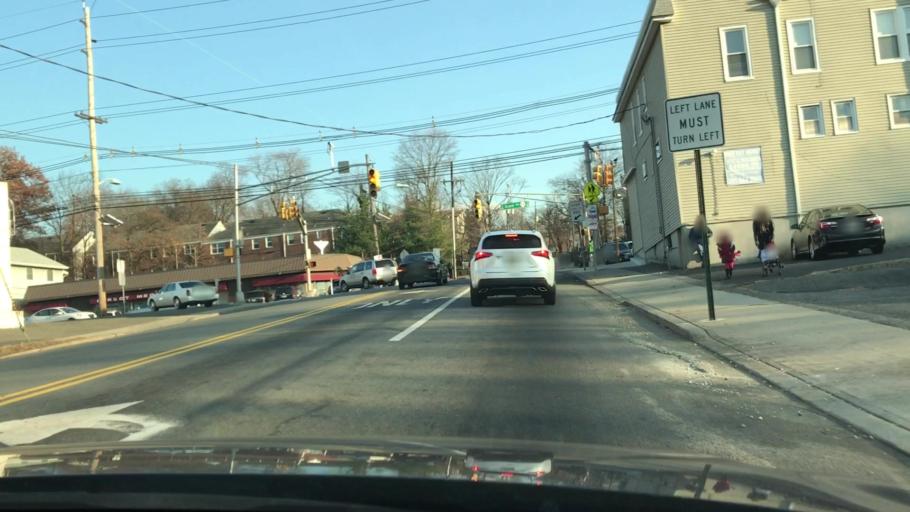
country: US
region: New Jersey
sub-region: Bergen County
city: Leonia
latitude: 40.8644
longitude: -73.9929
